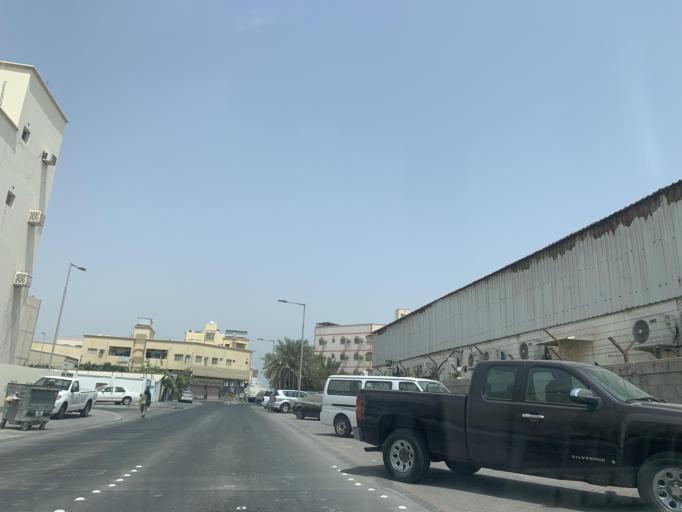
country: BH
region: Northern
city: Madinat `Isa
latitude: 26.1881
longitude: 50.5534
